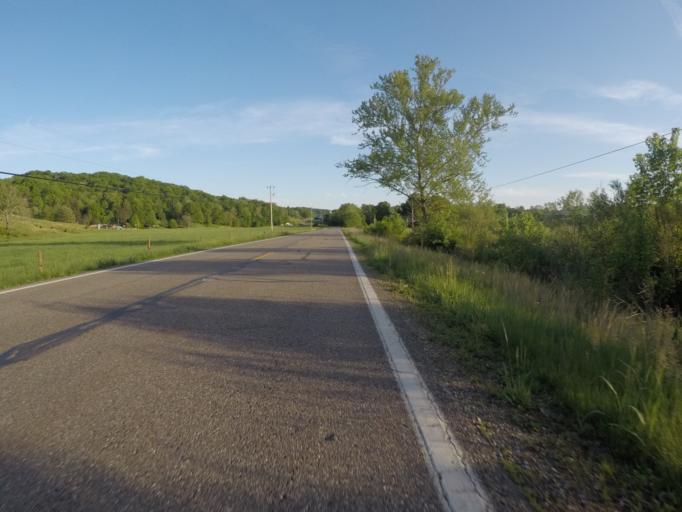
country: US
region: West Virginia
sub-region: Cabell County
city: Huntington
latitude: 38.5393
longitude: -82.4608
